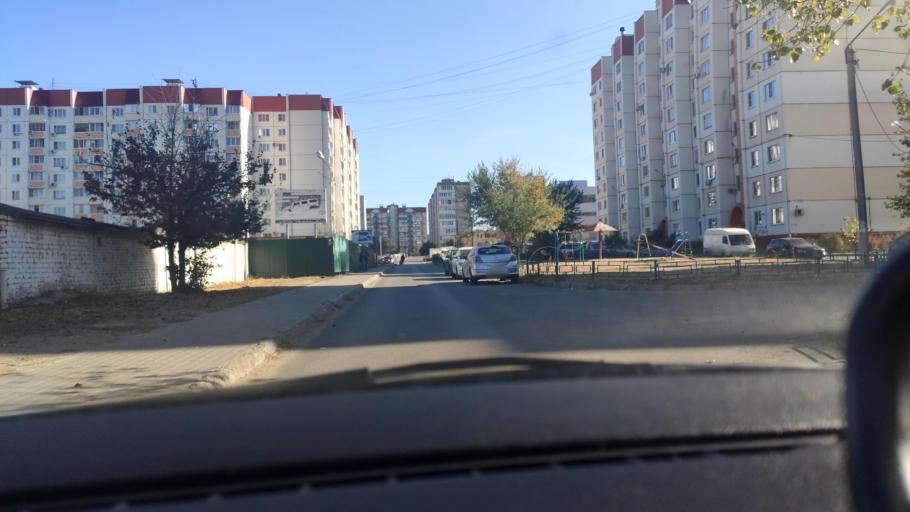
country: RU
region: Voronezj
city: Pridonskoy
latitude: 51.6254
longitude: 39.0748
